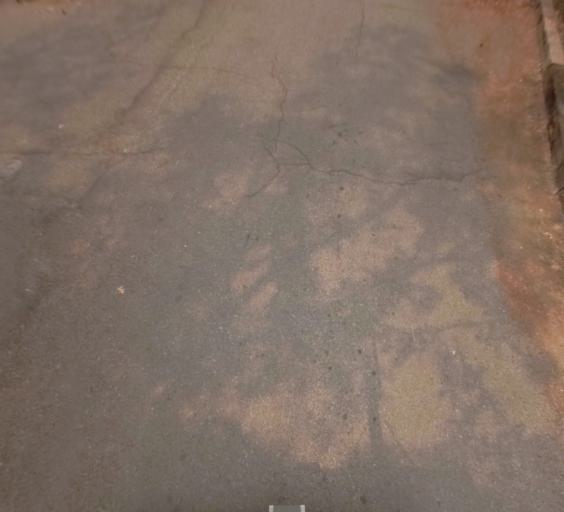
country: US
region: California
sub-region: Madera County
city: Oakhurst
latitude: 37.3170
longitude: -119.5542
